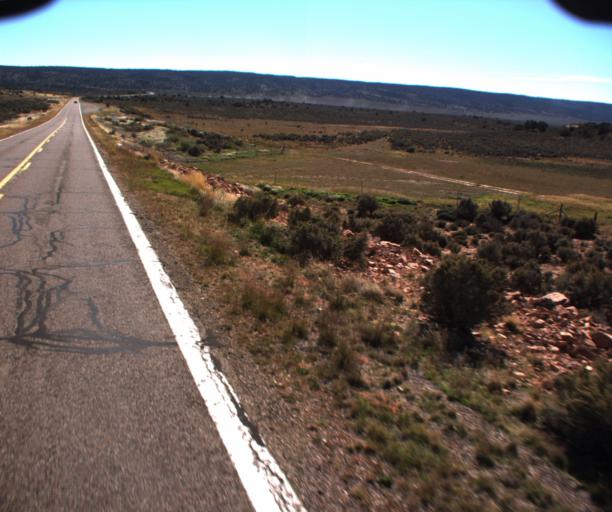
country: US
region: Arizona
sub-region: Coconino County
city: Fredonia
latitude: 36.8552
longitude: -112.2996
